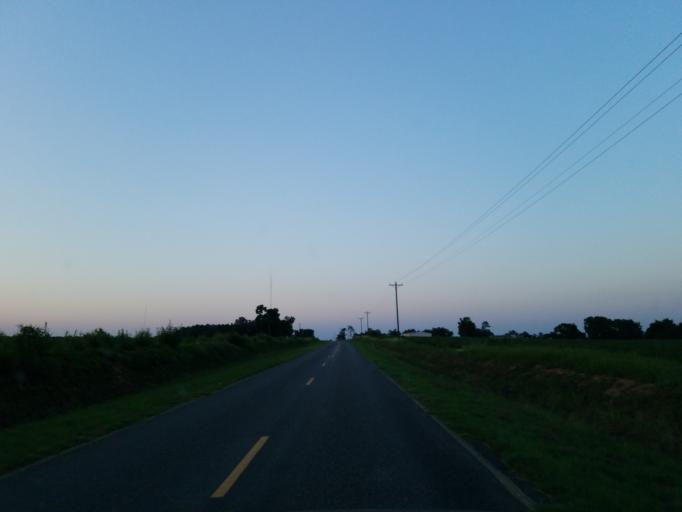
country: US
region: Georgia
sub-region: Dooly County
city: Vienna
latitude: 32.1749
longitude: -83.7985
